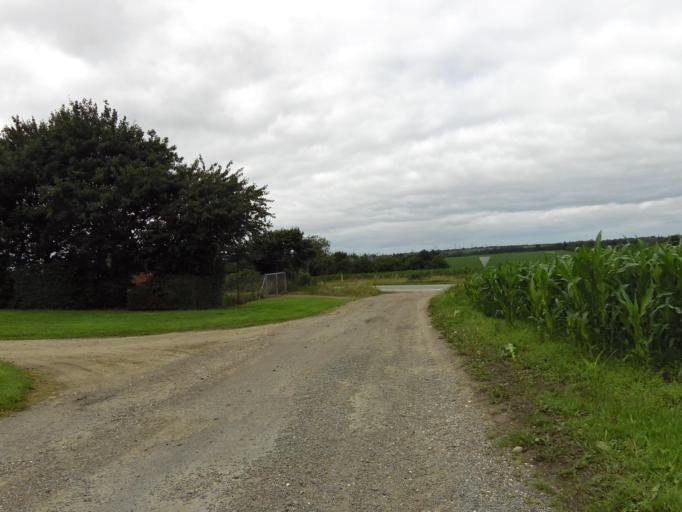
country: DK
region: South Denmark
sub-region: Haderslev Kommune
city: Gram
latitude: 55.2776
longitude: 9.1649
